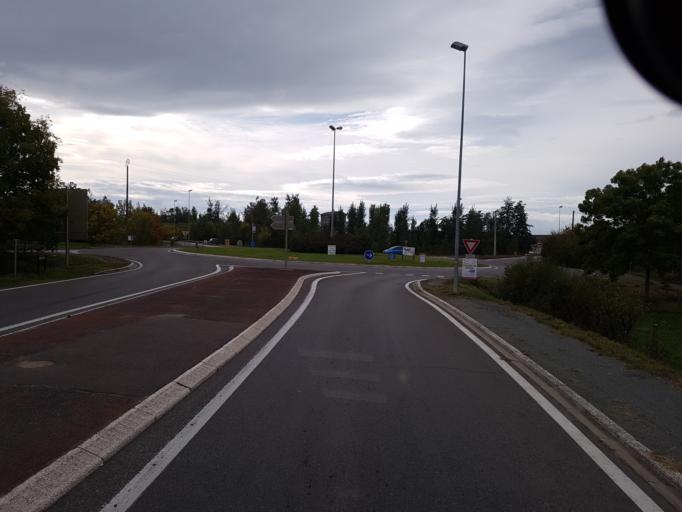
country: FR
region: Rhone-Alpes
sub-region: Departement de la Loire
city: Chamboeuf
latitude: 45.5746
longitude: 4.3039
